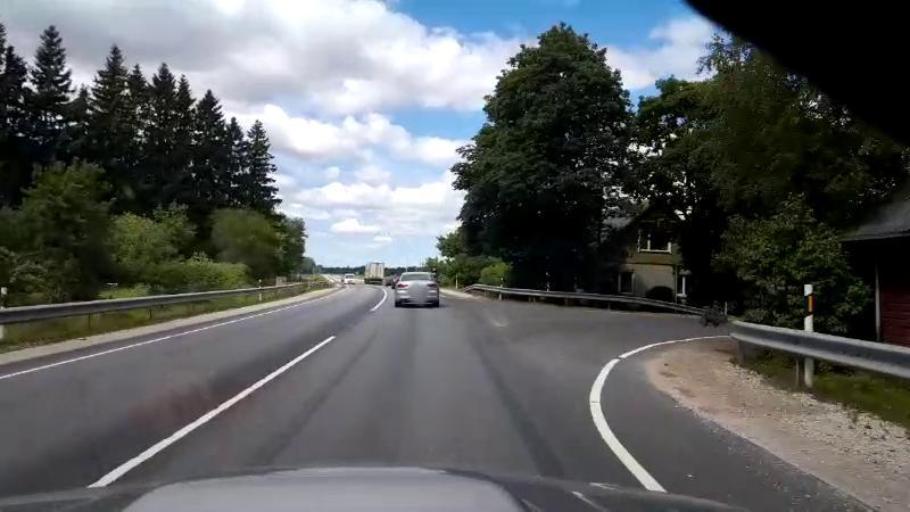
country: EE
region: Paernumaa
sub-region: Halinga vald
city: Parnu-Jaagupi
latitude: 58.6593
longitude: 24.4701
